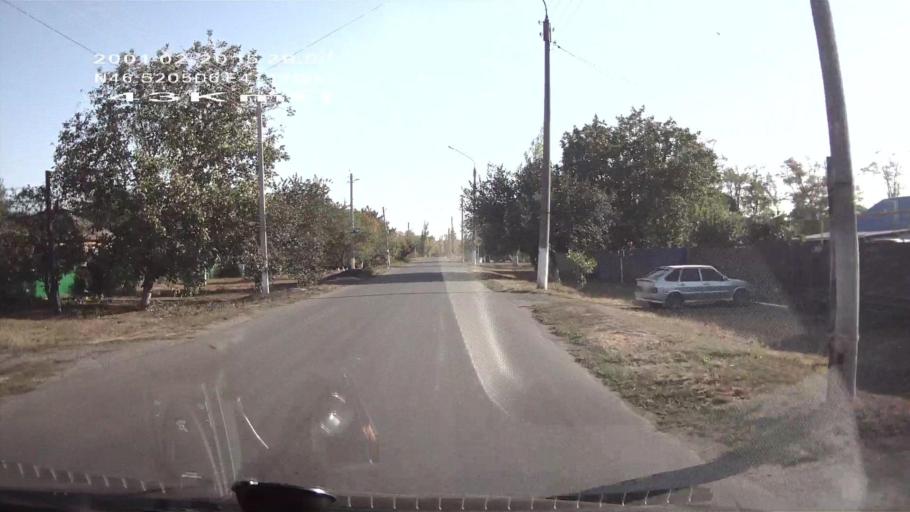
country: RU
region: Rostov
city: Gigant
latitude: 46.5204
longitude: 41.1913
